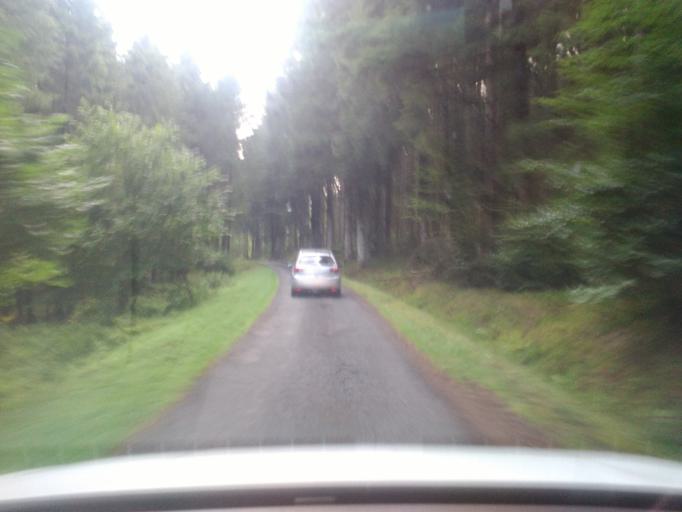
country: FR
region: Lorraine
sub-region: Departement des Vosges
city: Moyenmoutier
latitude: 48.4036
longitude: 6.9100
